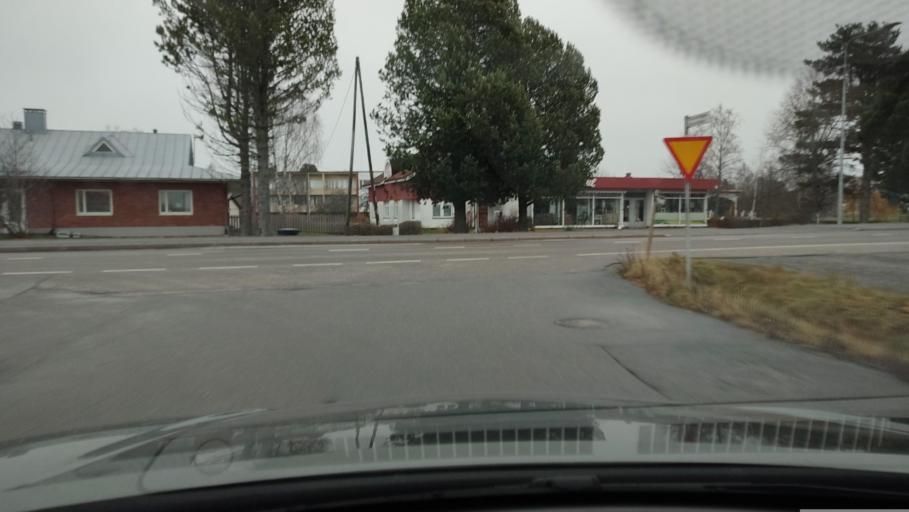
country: FI
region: Ostrobothnia
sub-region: Sydosterbotten
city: Kristinestad
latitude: 62.2540
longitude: 21.5083
